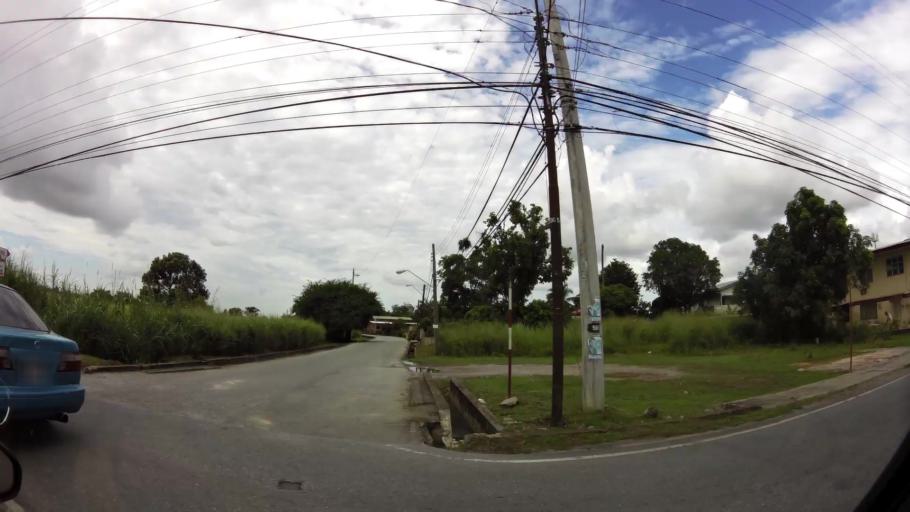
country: TT
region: Chaguanas
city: Chaguanas
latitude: 10.4941
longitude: -61.4081
